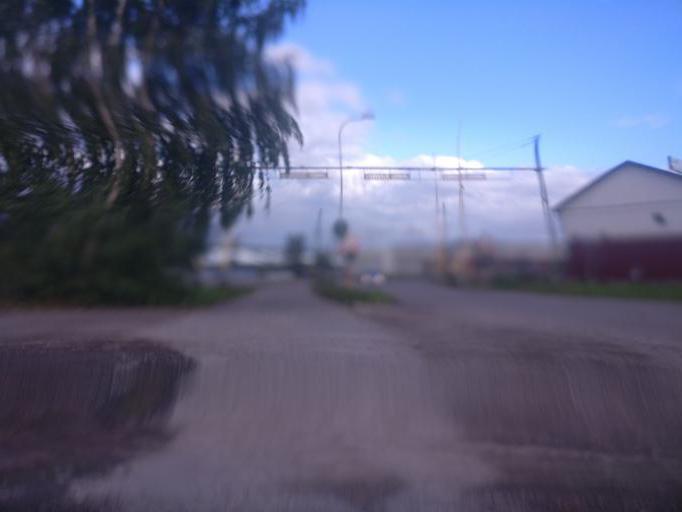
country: SE
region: Vaesternorrland
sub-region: Sundsvalls Kommun
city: Sundsvall
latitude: 62.3863
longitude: 17.3270
